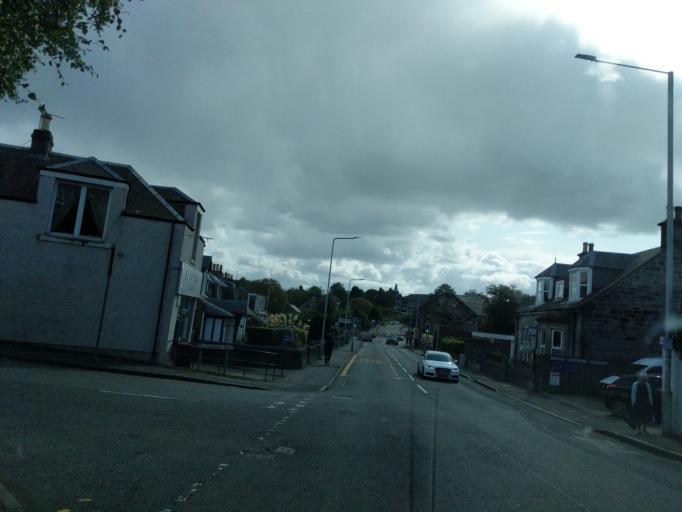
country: GB
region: Scotland
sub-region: Fife
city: Dunfermline
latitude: 56.0751
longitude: -3.4514
